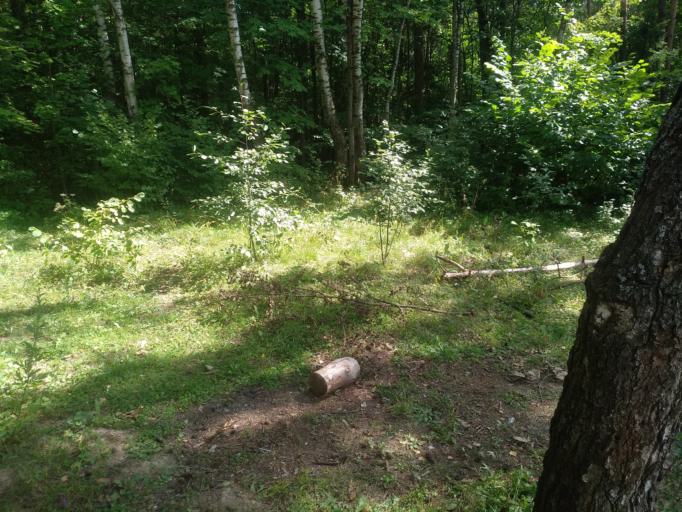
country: RU
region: Moskovskaya
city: Dedovsk
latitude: 55.8747
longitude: 37.0901
